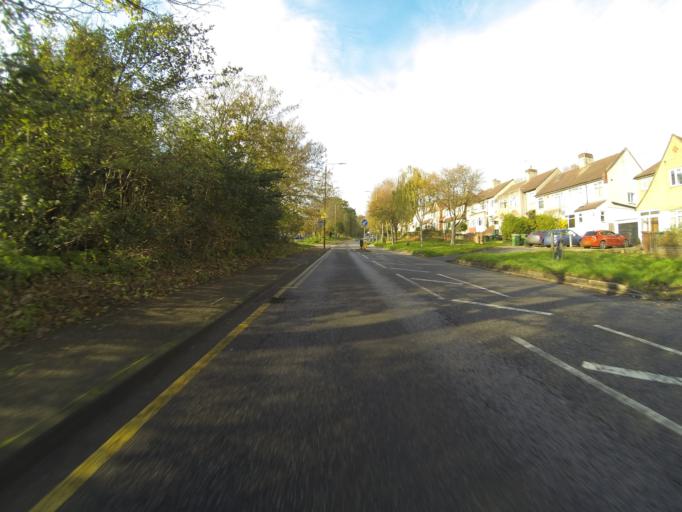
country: GB
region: England
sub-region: Greater London
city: Bexley
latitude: 51.4533
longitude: 0.1633
